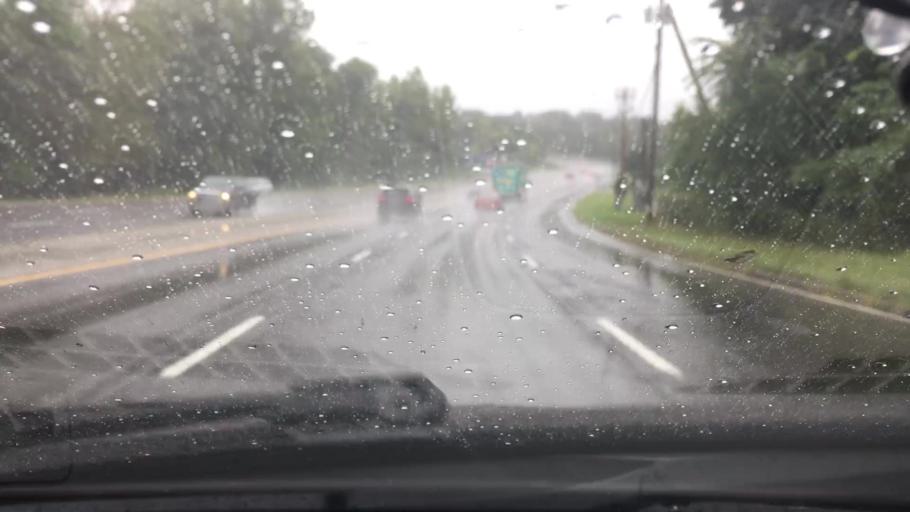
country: US
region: New York
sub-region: Dutchess County
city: Spackenkill
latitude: 41.6416
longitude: -73.9200
